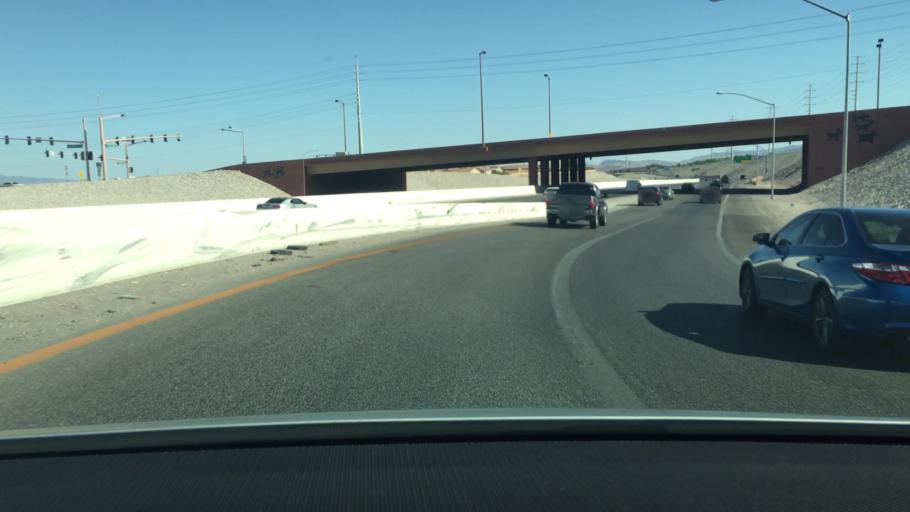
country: US
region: Nevada
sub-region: Clark County
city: Summerlin South
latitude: 36.1929
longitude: -115.3427
